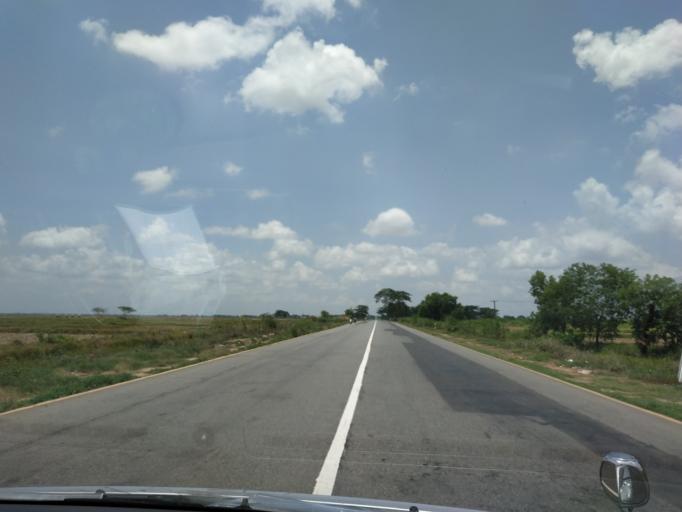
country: MM
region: Bago
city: Bago
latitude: 17.4623
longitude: 96.5938
